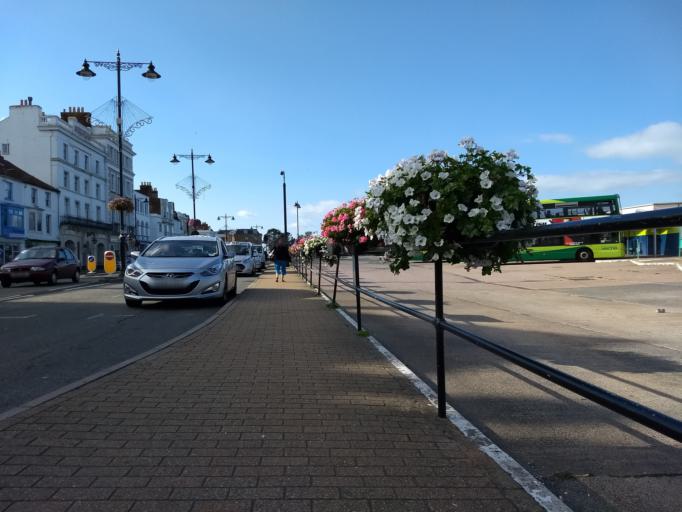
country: GB
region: England
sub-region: Isle of Wight
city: Ryde
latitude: 50.7324
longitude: -1.1589
